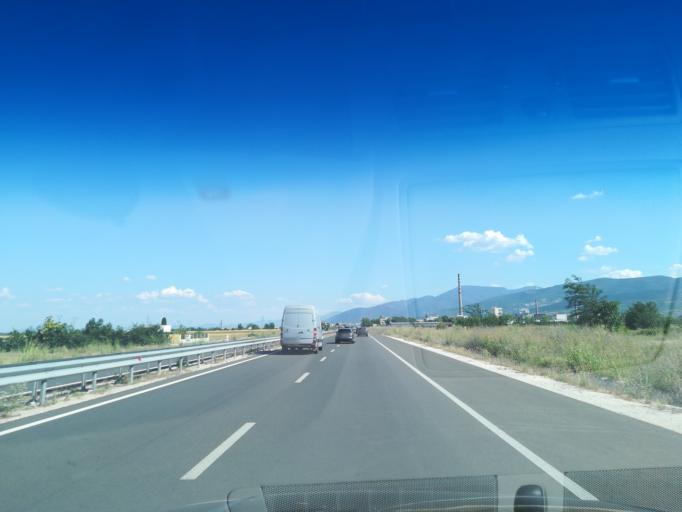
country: BG
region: Plovdiv
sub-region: Obshtina Asenovgrad
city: Asenovgrad
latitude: 42.0743
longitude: 24.8072
